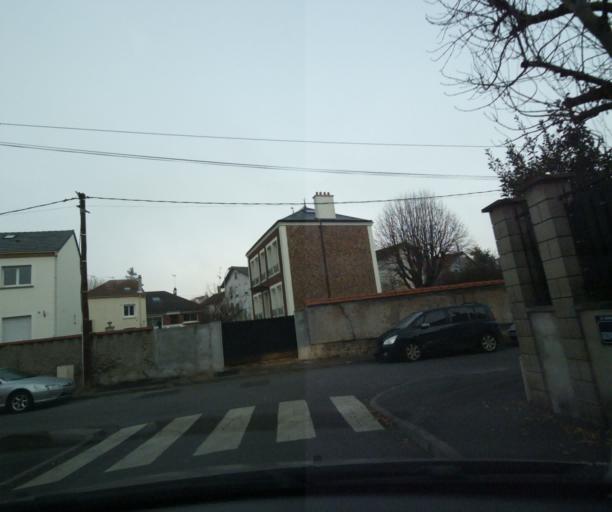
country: FR
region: Ile-de-France
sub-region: Departement du Val-de-Marne
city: Le Perreux-sur-Marne
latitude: 48.8563
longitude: 2.5016
